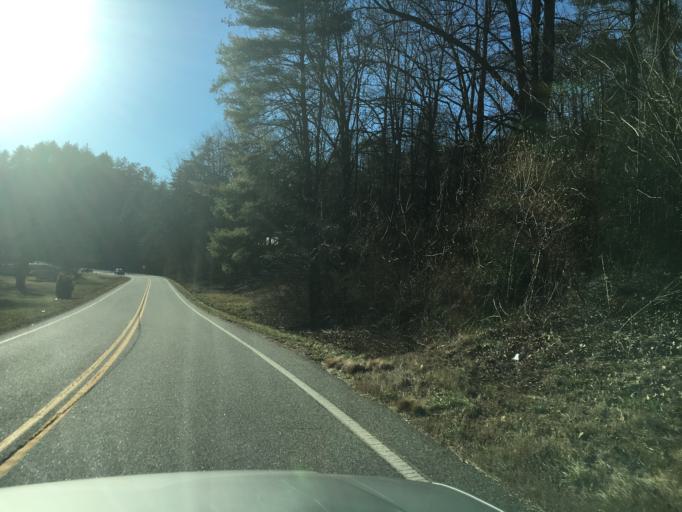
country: US
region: Georgia
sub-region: White County
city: Cleveland
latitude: 34.6782
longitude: -83.8989
